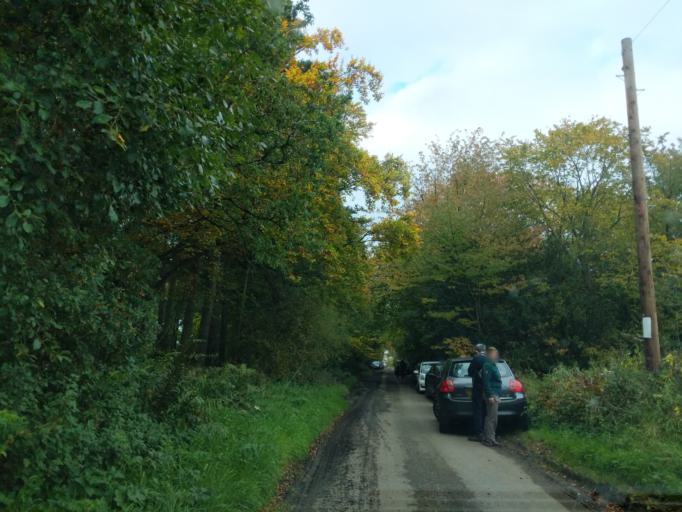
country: GB
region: Scotland
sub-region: East Lothian
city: Macmerry
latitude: 55.9454
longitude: -2.8664
